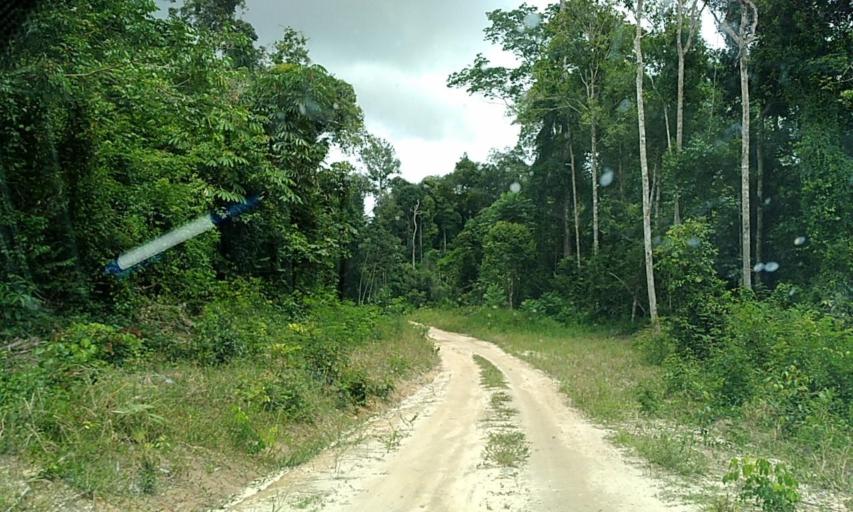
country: BR
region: Para
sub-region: Altamira
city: Altamira
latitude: -3.0614
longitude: -52.9088
